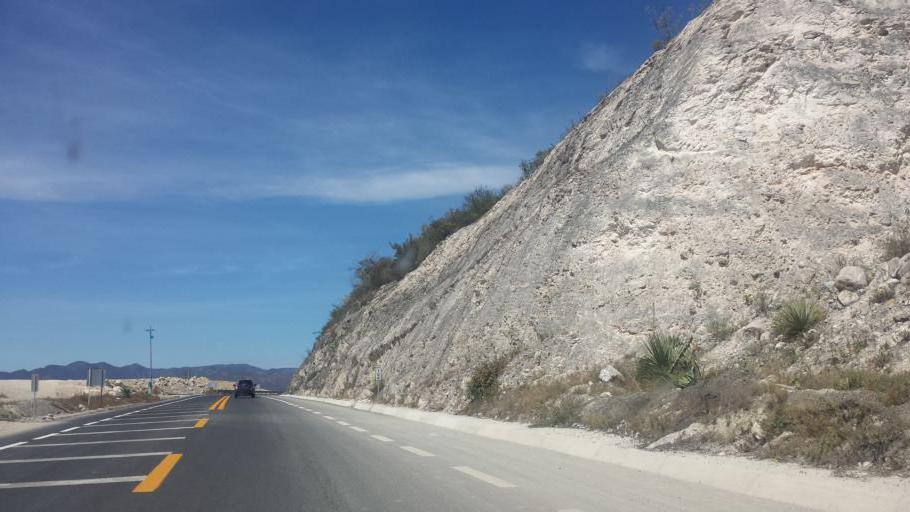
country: MX
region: Puebla
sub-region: San Jose Miahuatlan
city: San Pedro Tetitlan
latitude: 18.0548
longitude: -97.3536
